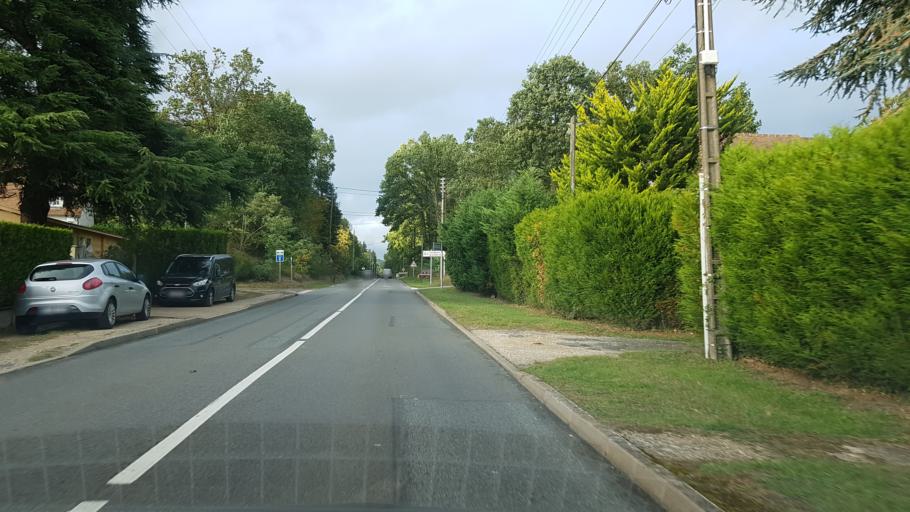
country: FR
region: Ile-de-France
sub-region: Departement de l'Essonne
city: Fontenay-les-Briis
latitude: 48.6182
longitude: 2.1701
